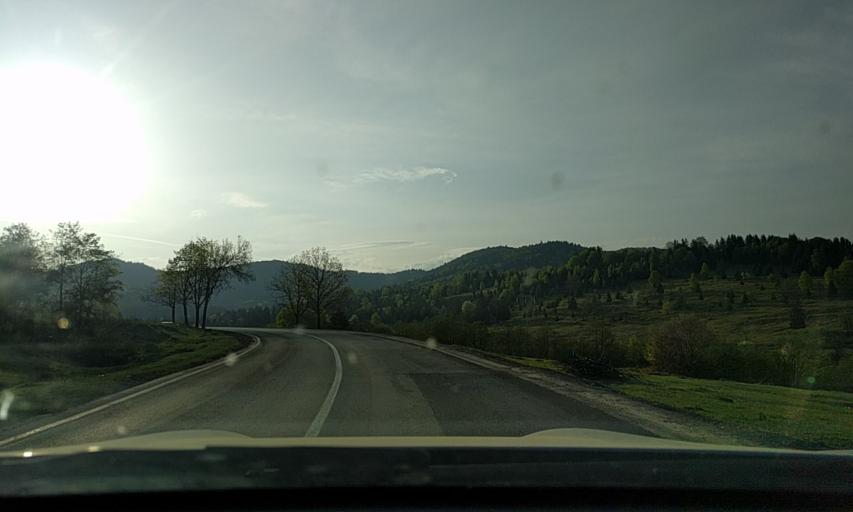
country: RO
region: Covasna
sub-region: Comuna Bretcu
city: Bretcu
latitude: 46.0437
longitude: 26.3313
